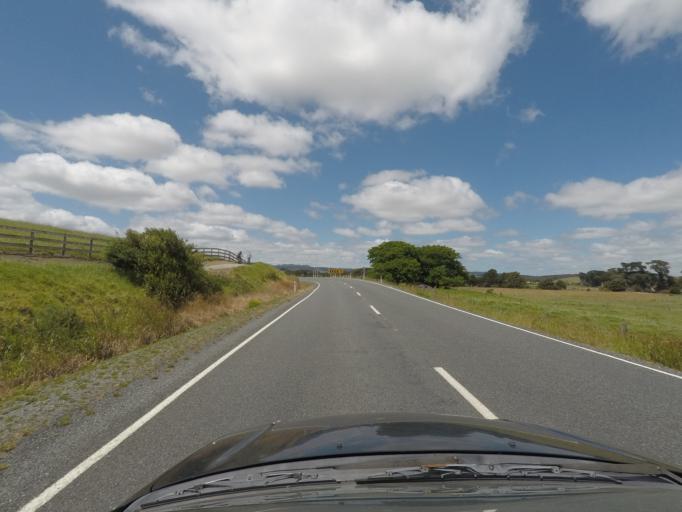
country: NZ
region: Northland
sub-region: Whangarei
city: Ruakaka
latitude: -35.9891
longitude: 174.4566
